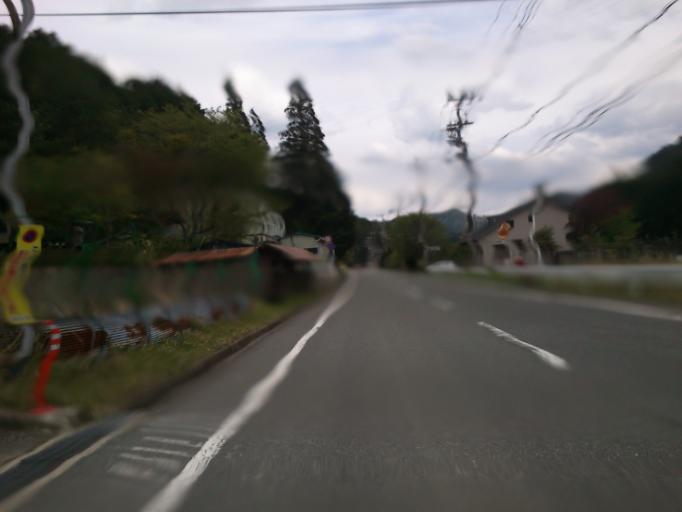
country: JP
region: Kyoto
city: Kameoka
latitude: 35.2074
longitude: 135.5959
